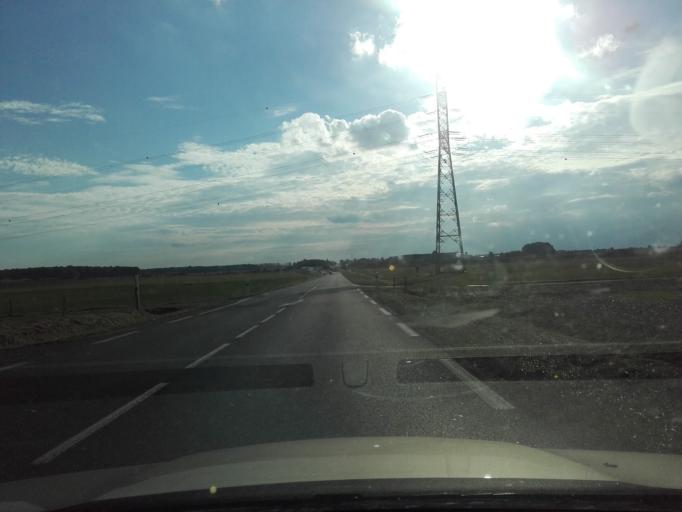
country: FR
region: Centre
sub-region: Departement d'Indre-et-Loire
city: Monnaie
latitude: 47.4796
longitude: 0.7630
